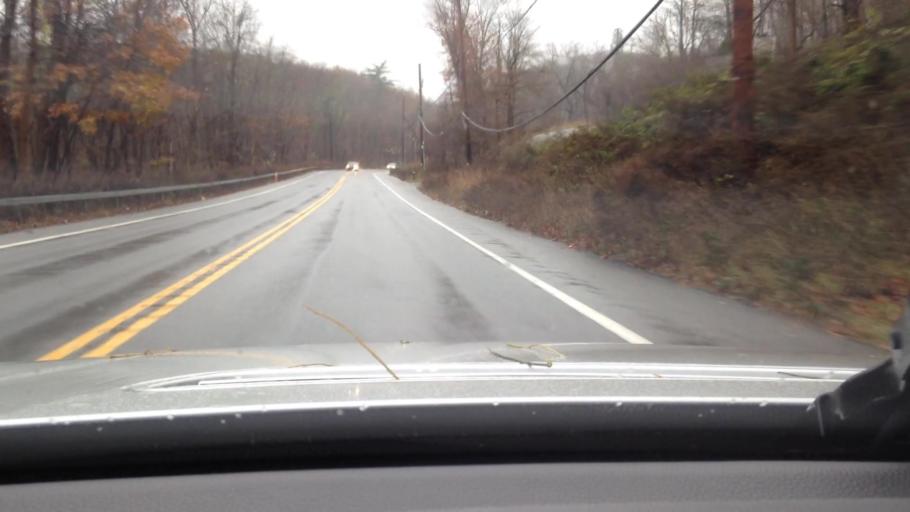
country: US
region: New York
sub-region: Westchester County
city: Peekskill
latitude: 41.3307
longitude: -73.9254
